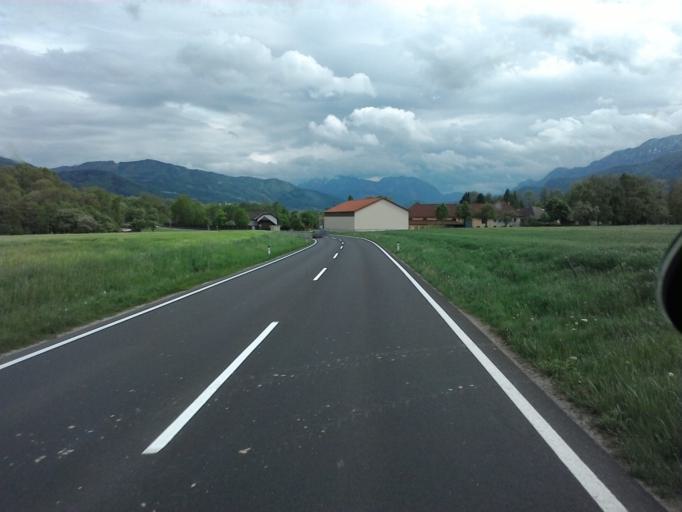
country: AT
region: Upper Austria
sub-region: Politischer Bezirk Kirchdorf an der Krems
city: Micheldorf in Oberoesterreich
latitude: 47.9256
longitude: 14.0897
